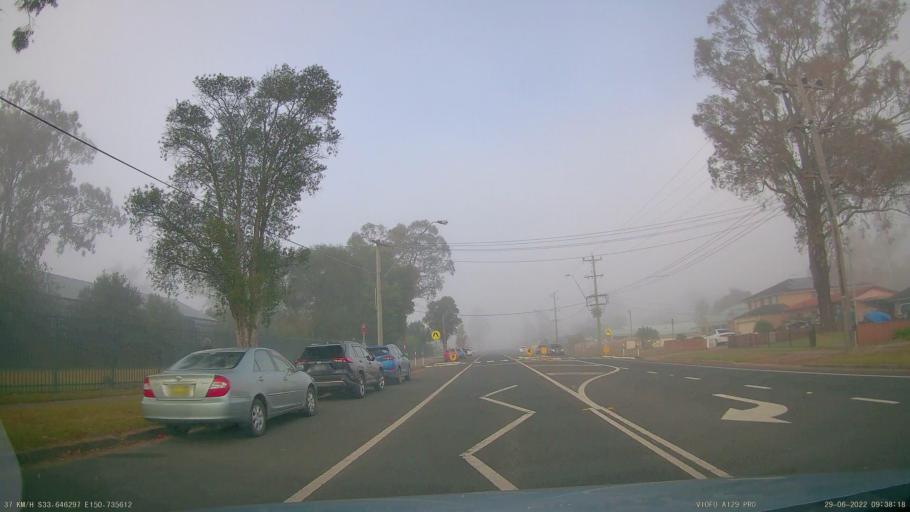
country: AU
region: New South Wales
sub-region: Hawkesbury
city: Richmond
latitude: -33.6466
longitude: 150.7355
